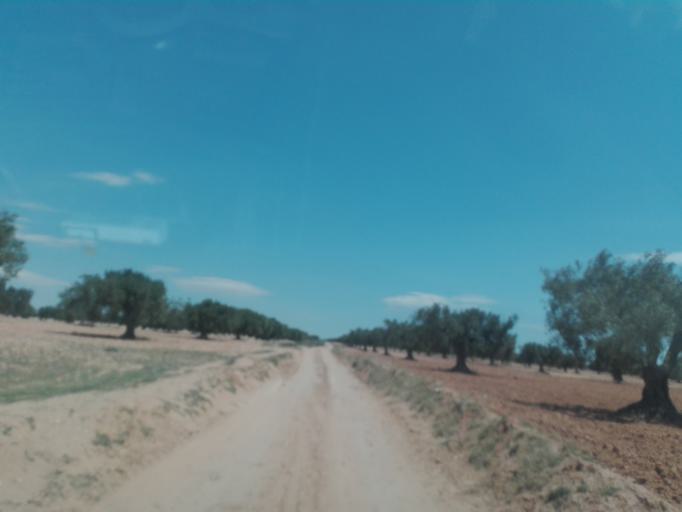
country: TN
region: Safaqis
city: Sfax
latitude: 34.6557
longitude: 10.5958
